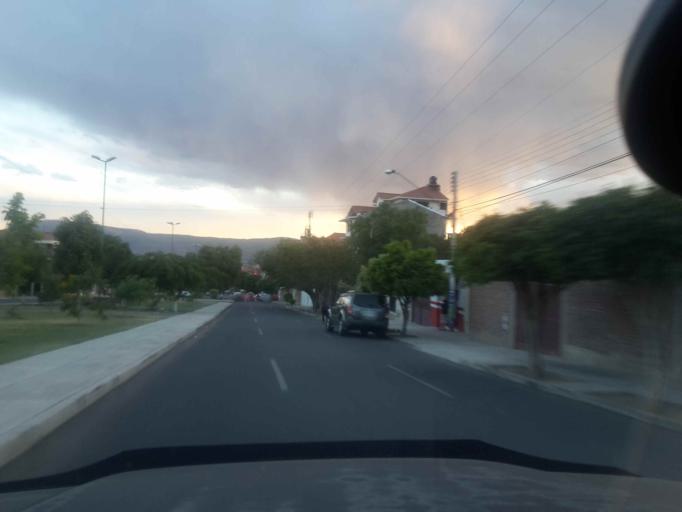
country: BO
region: Cochabamba
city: Cochabamba
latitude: -17.3589
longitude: -66.1697
